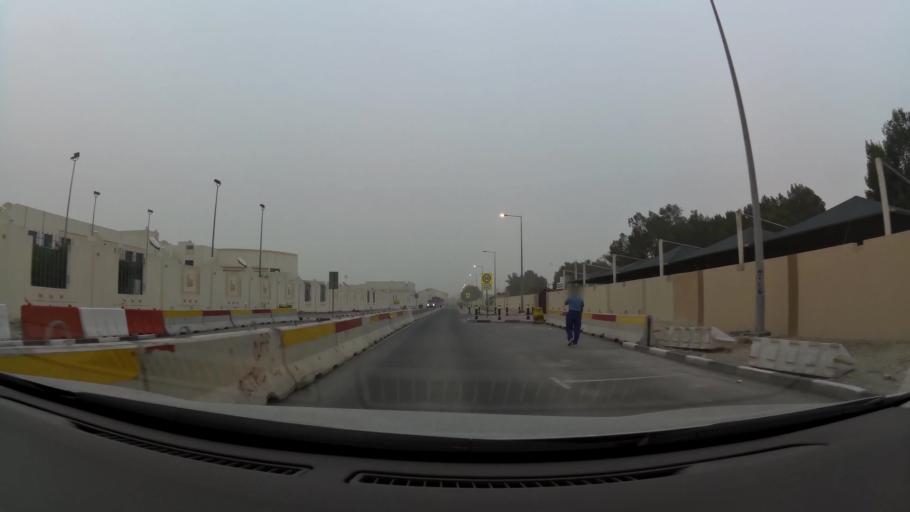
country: QA
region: Baladiyat ad Dawhah
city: Doha
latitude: 25.2318
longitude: 51.5033
